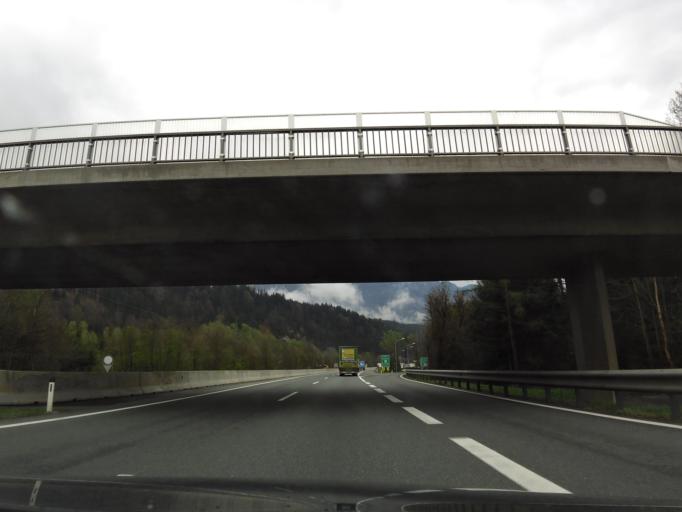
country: AT
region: Tyrol
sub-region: Politischer Bezirk Kufstein
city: Angath
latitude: 47.5149
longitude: 12.0650
